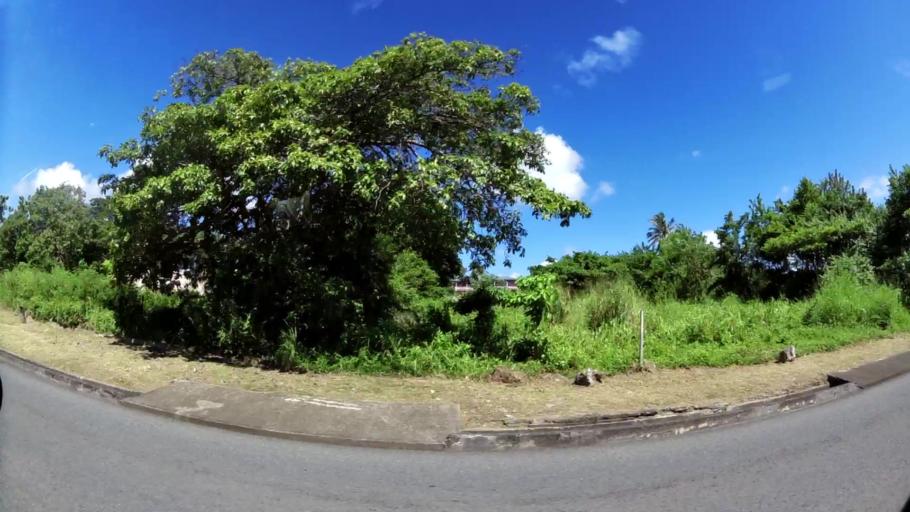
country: TT
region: Tobago
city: Scarborough
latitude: 11.1688
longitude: -60.7762
